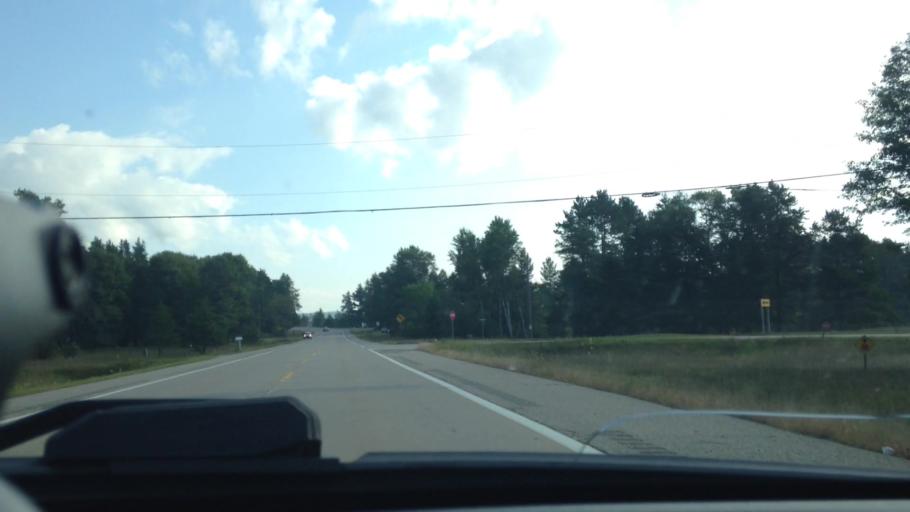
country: US
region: Michigan
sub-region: Dickinson County
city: Norway
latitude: 45.7672
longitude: -87.9142
